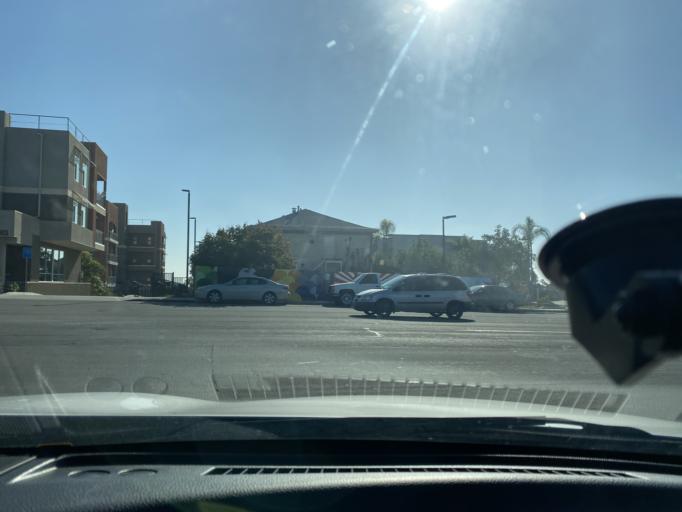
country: US
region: California
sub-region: San Diego County
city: National City
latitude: 32.7042
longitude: -117.0868
